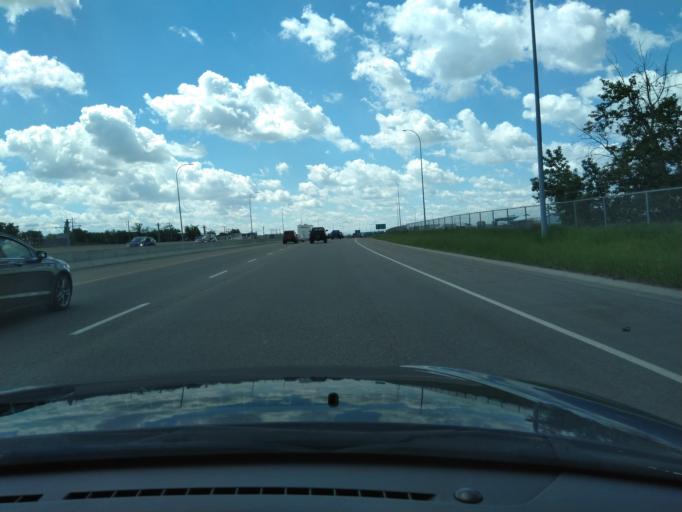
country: CA
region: Alberta
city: Calgary
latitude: 51.1163
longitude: -113.9709
